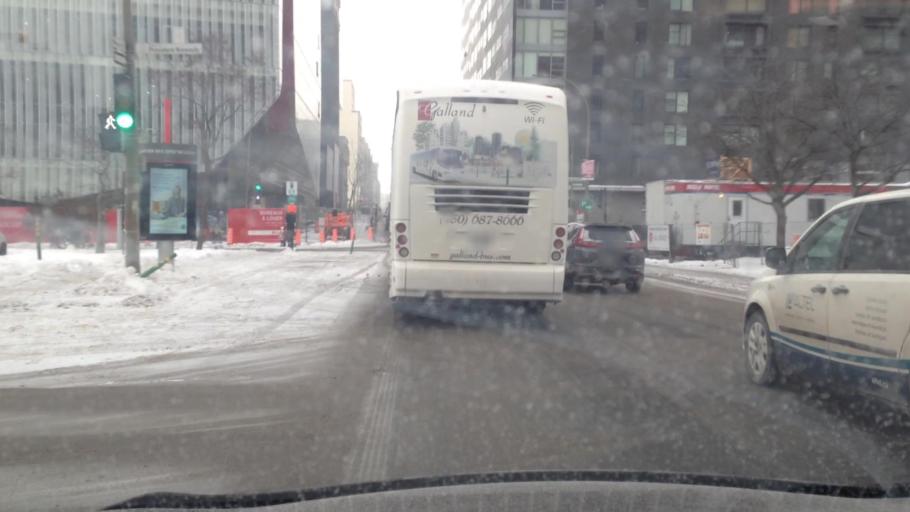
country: CA
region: Quebec
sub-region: Montreal
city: Montreal
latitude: 45.5076
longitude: -73.5695
